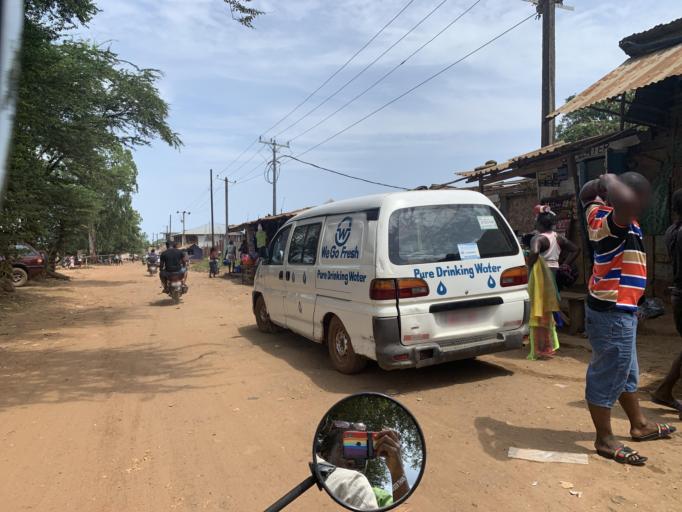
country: SL
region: Western Area
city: Hastings
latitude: 8.3943
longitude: -13.1436
